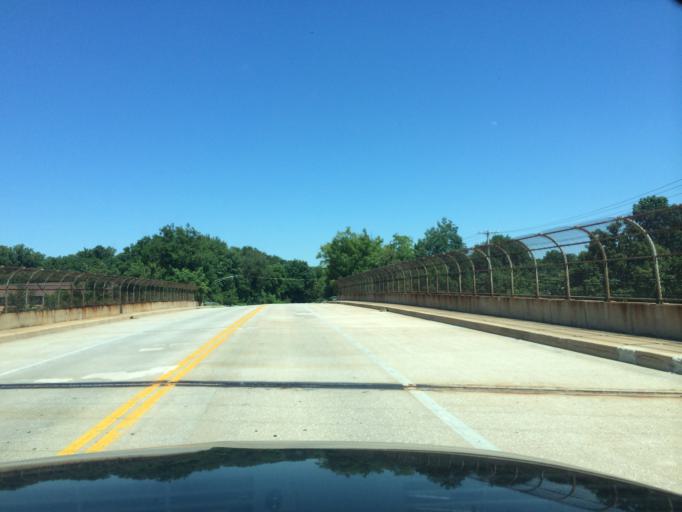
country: US
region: Maryland
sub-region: Baltimore County
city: Lutherville
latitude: 39.4242
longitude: -76.6385
